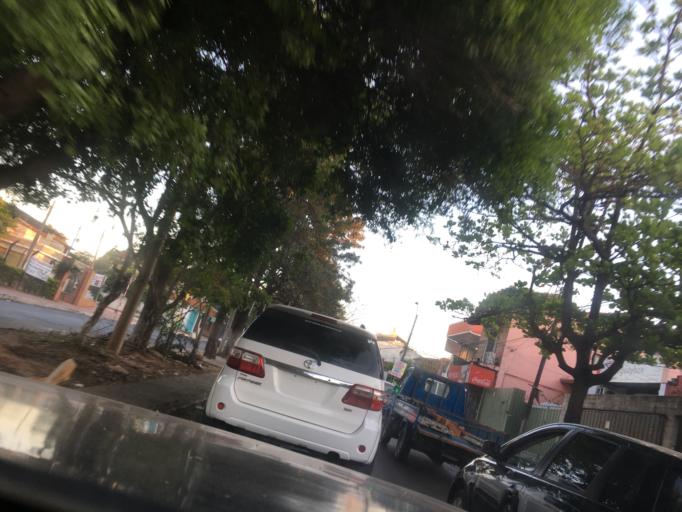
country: PY
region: Central
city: Lambare
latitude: -25.3342
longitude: -57.6076
